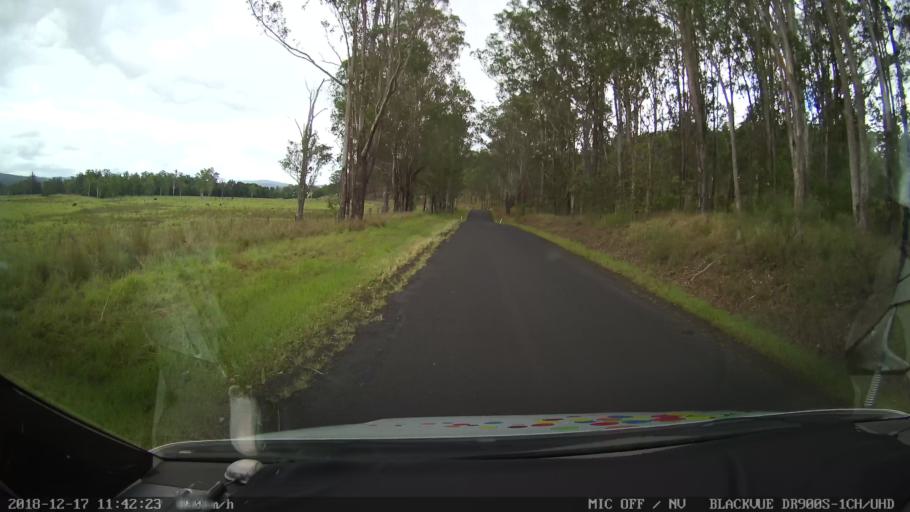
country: AU
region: New South Wales
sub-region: Kyogle
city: Kyogle
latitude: -28.6690
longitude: 152.5909
